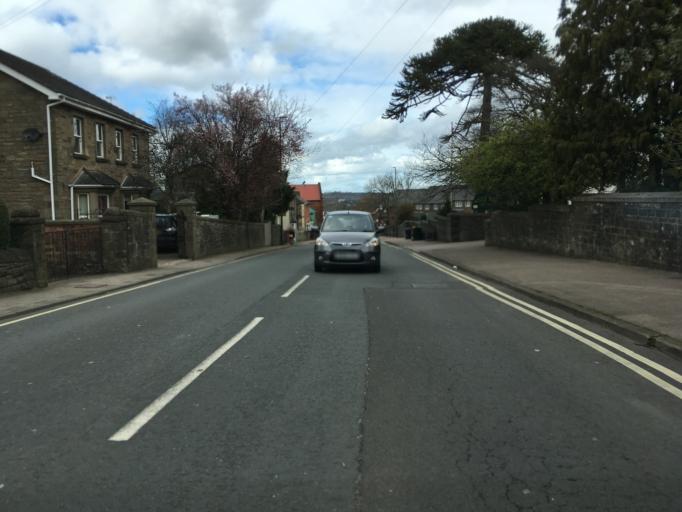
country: GB
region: England
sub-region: Gloucestershire
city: Cinderford
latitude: 51.8225
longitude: -2.4969
